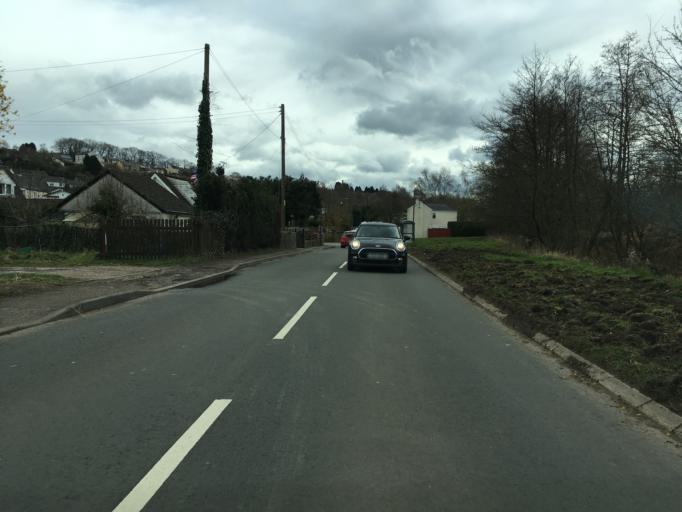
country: GB
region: England
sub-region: Gloucestershire
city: Cinderford
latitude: 51.8186
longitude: -2.5085
